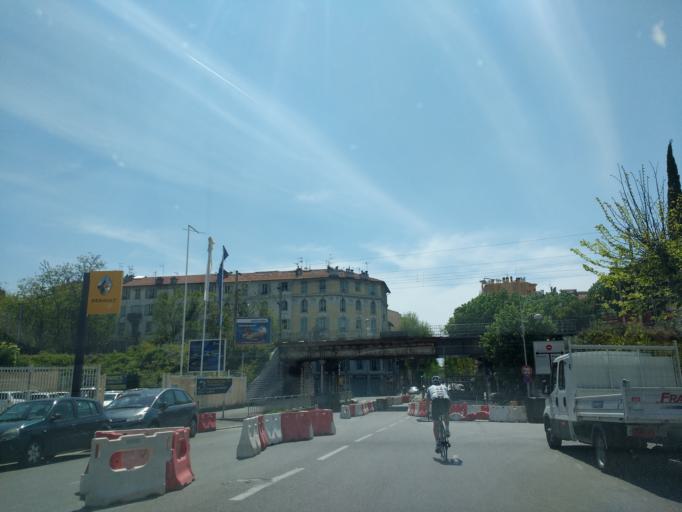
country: FR
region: Provence-Alpes-Cote d'Azur
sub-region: Departement des Alpes-Maritimes
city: Villefranche-sur-Mer
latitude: 43.7058
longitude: 7.2915
